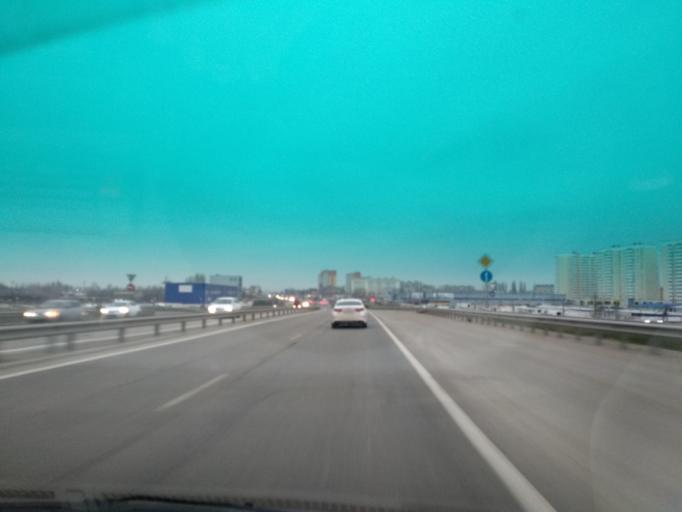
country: RU
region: Krasnodarskiy
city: Pashkovskiy
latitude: 45.0417
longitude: 39.1281
